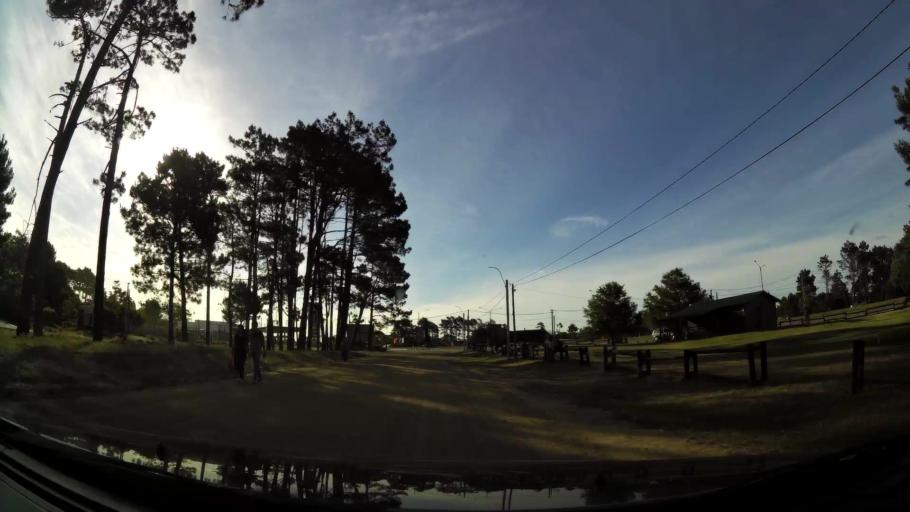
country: UY
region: Canelones
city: Empalme Olmos
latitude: -34.7791
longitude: -55.8603
